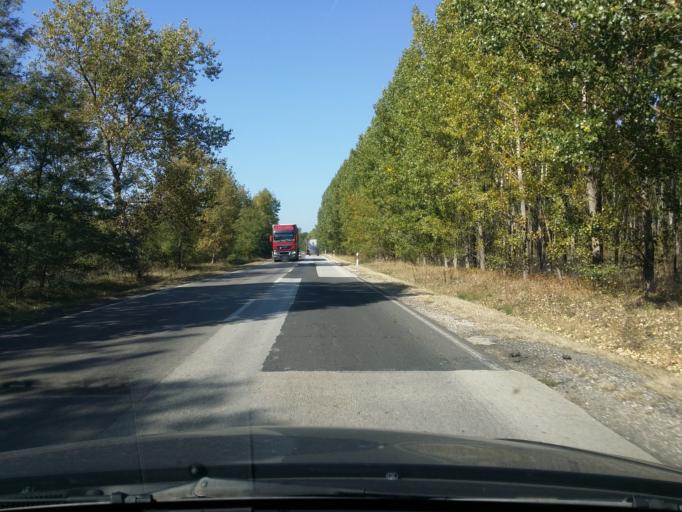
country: HU
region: Bacs-Kiskun
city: Nyarlorinc
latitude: 46.8873
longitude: 19.8367
